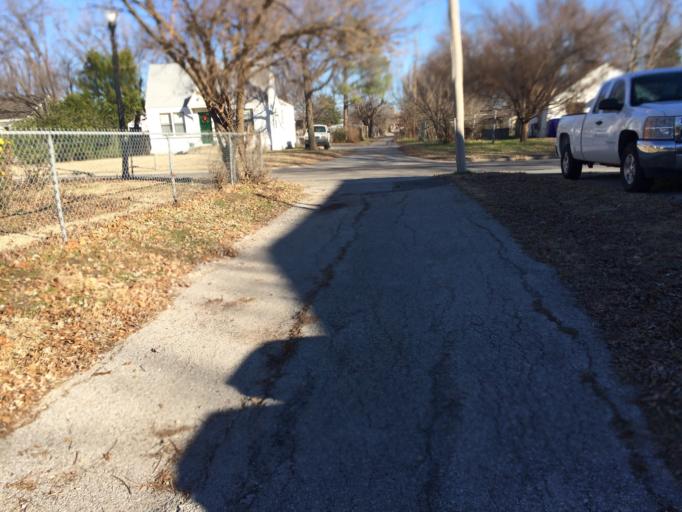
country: US
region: Oklahoma
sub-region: Cleveland County
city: Norman
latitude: 35.2310
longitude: -97.4465
